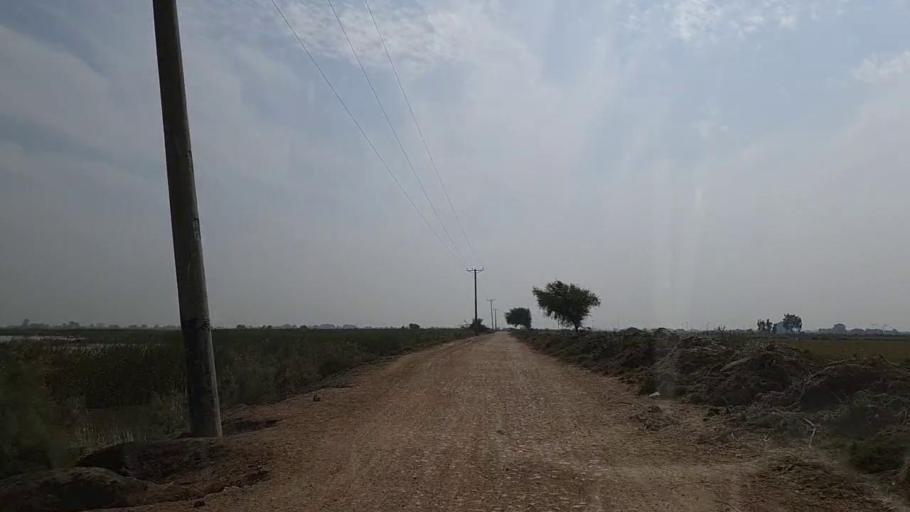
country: PK
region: Sindh
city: Mirpur Batoro
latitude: 24.6032
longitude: 68.2126
